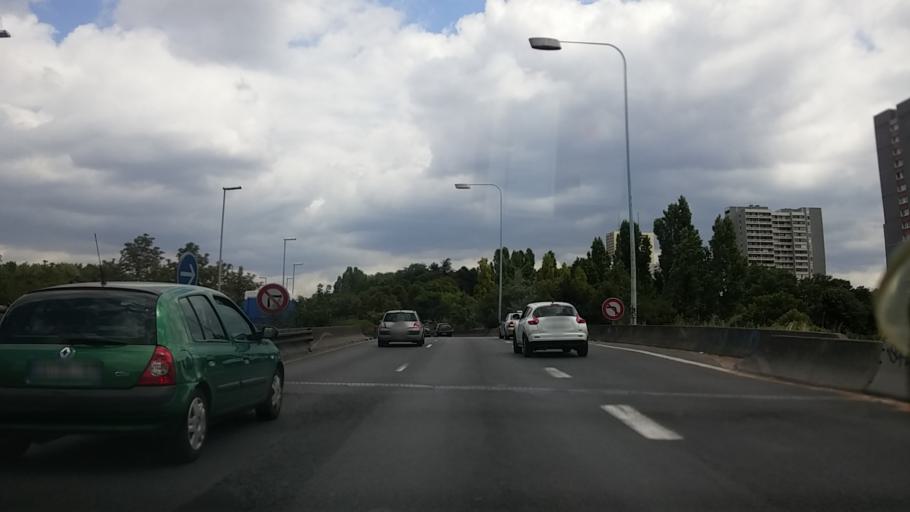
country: FR
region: Ile-de-France
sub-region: Departement de Seine-Saint-Denis
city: Bagnolet
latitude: 48.8651
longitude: 2.4178
